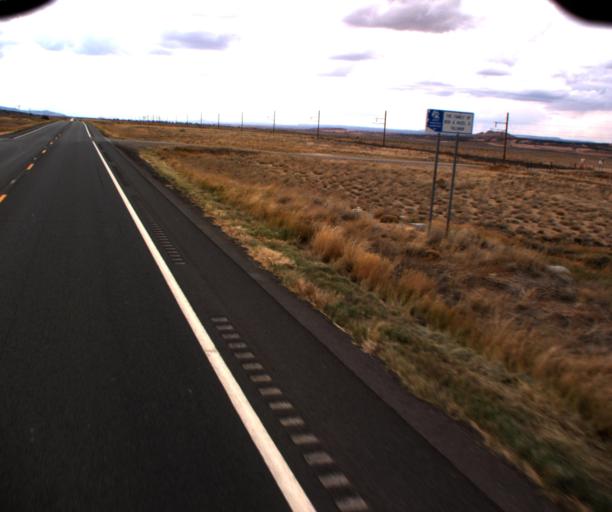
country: US
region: Arizona
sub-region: Navajo County
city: Kayenta
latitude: 36.5305
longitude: -110.5683
